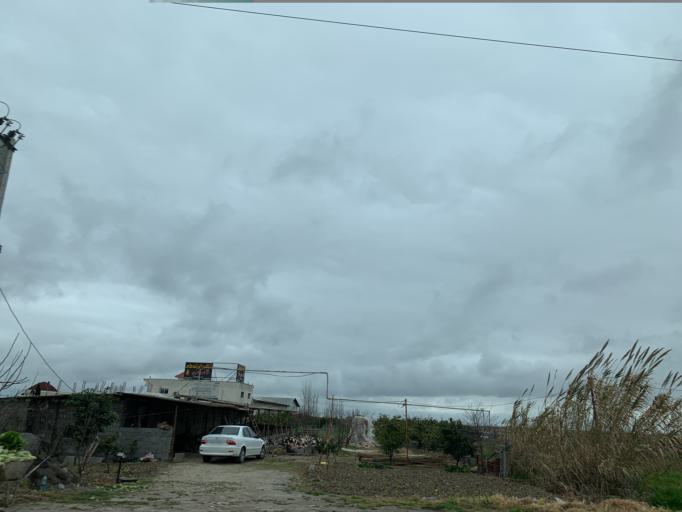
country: IR
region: Mazandaran
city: Babol
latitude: 36.5113
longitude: 52.5551
